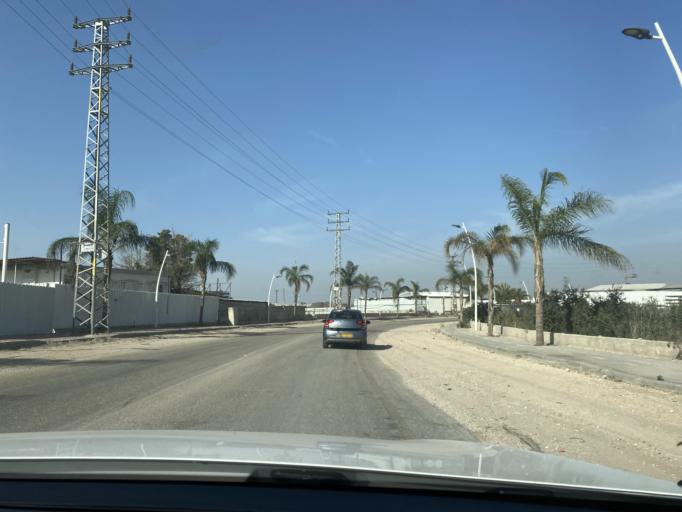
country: IL
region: Central District
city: Jaljulya
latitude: 32.1374
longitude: 34.9620
